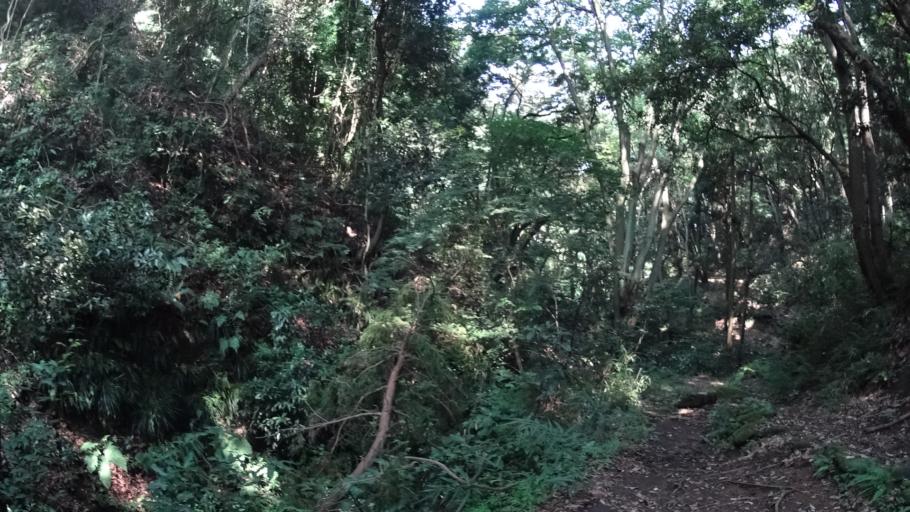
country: JP
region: Kanagawa
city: Zushi
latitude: 35.3053
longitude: 139.6043
